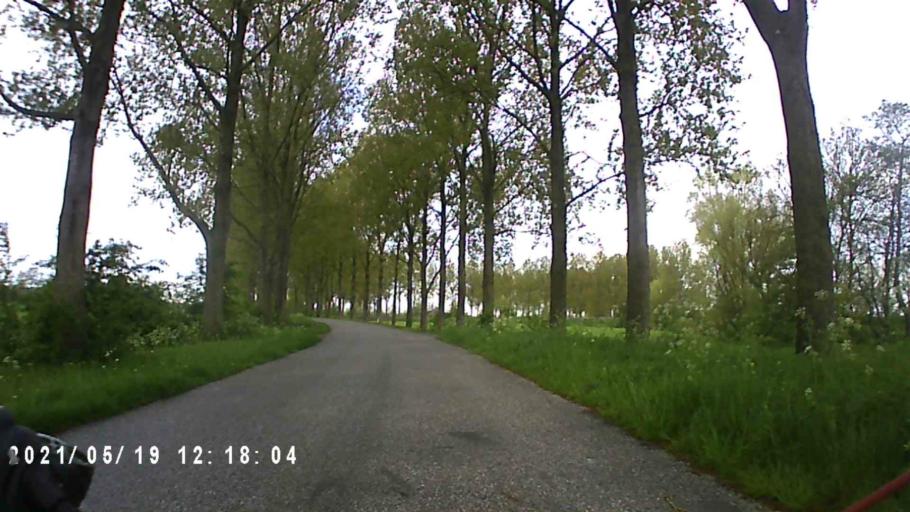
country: NL
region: Friesland
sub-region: Gemeente Kollumerland en Nieuwkruisland
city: Kollum
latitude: 53.2598
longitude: 6.1731
